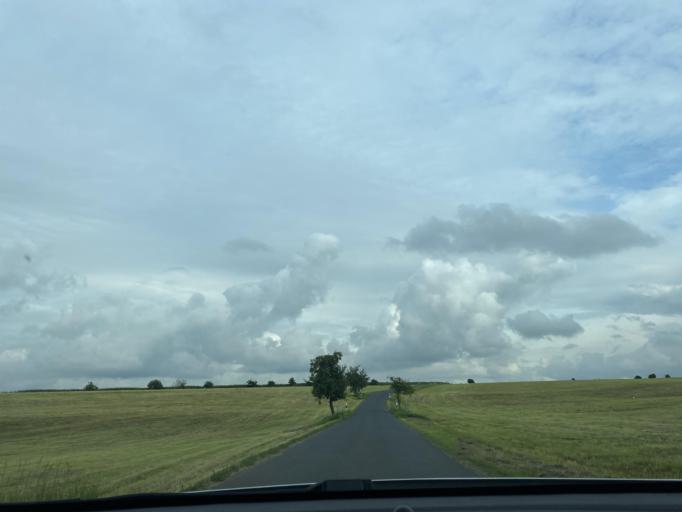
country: DE
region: Saxony
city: Herrnhut
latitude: 51.0228
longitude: 14.7594
